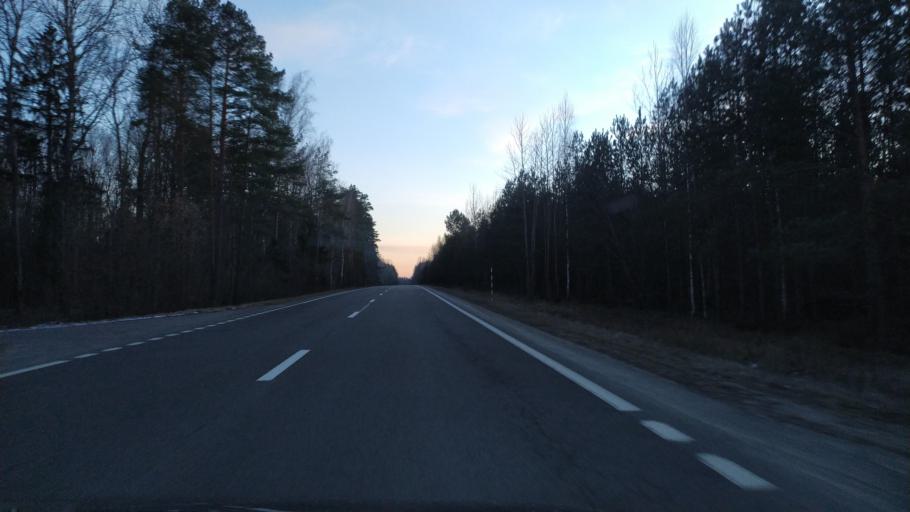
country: BY
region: Brest
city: Pruzhany
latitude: 52.5140
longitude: 24.1797
